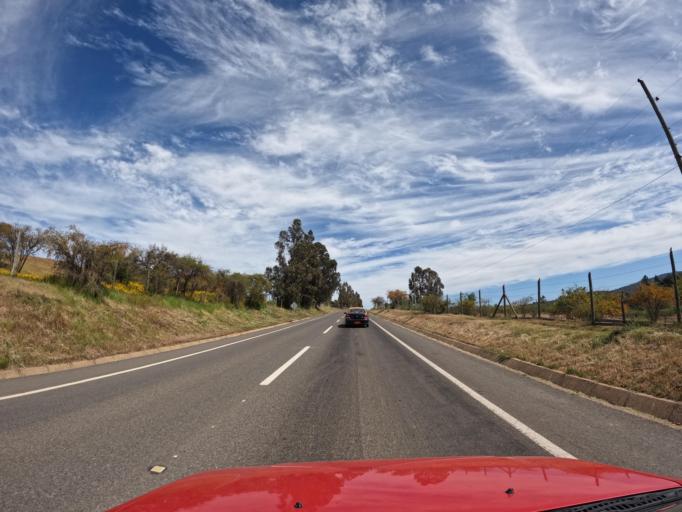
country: CL
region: Maule
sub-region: Provincia de Talca
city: Talca
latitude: -35.1202
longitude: -71.9583
